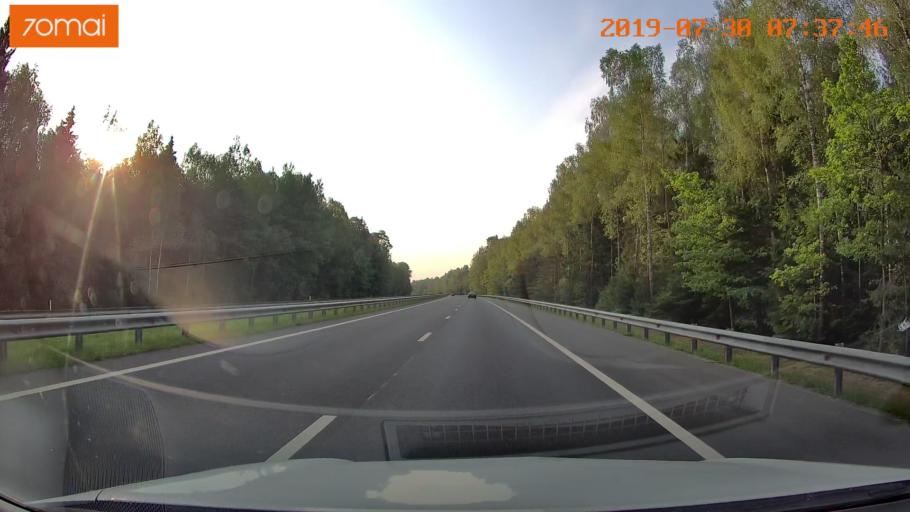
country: RU
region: Kaliningrad
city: Gvardeysk
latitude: 54.6537
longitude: 21.1517
